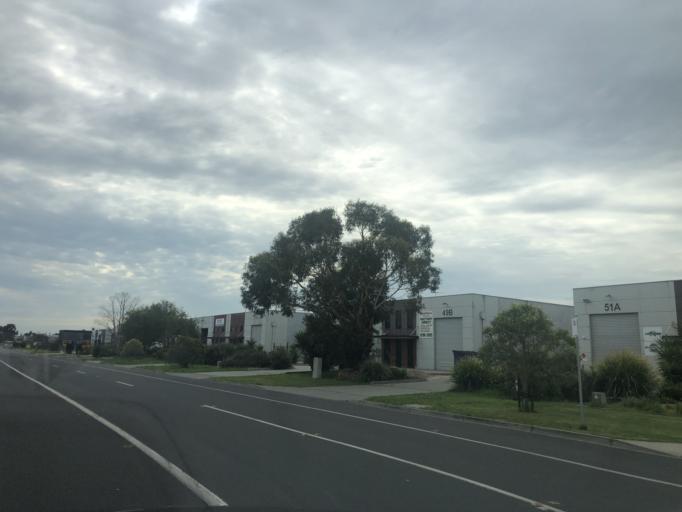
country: AU
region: Victoria
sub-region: Casey
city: Hallam
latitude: -38.0196
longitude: 145.2790
